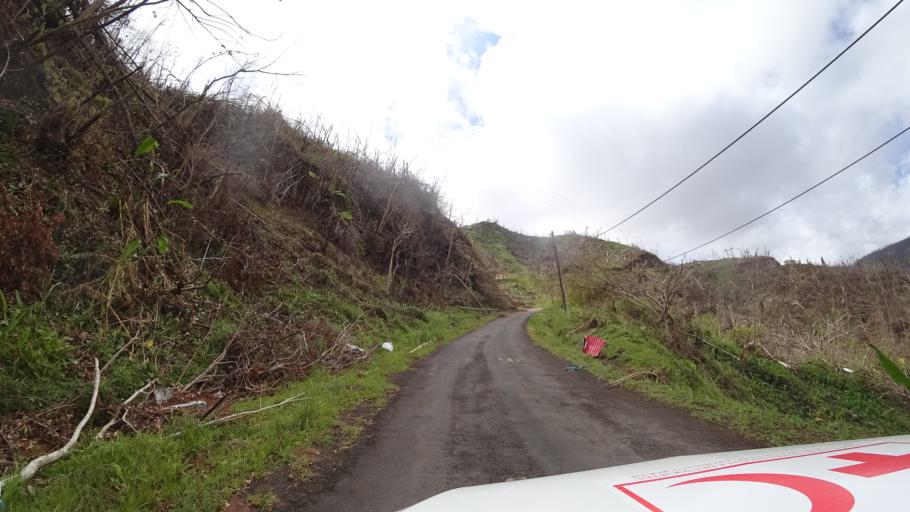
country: DM
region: Saint David
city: Rosalie
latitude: 15.3975
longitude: -61.2588
